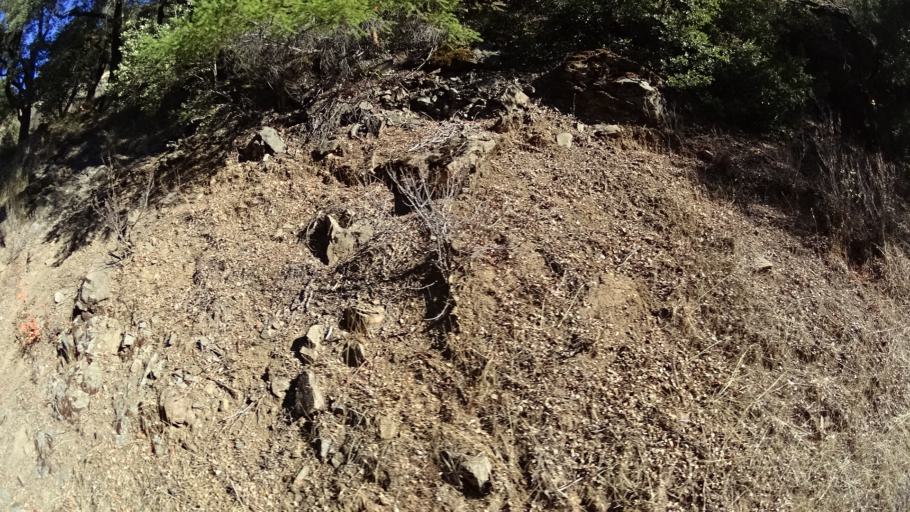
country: US
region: California
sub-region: Humboldt County
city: Willow Creek
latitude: 41.2007
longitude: -123.2221
